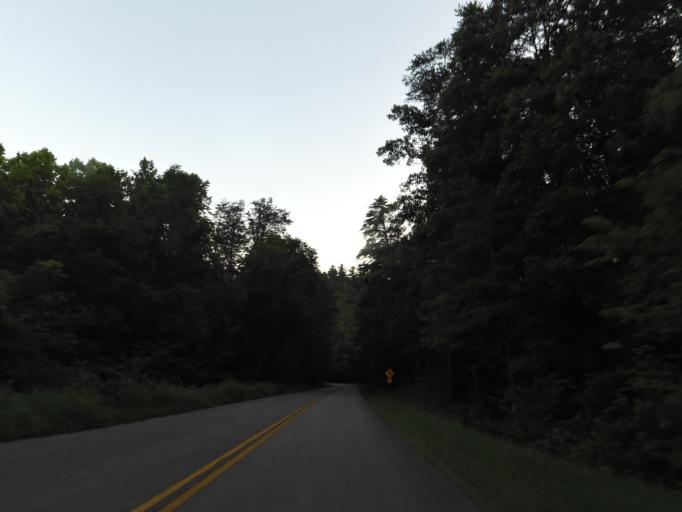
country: US
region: Tennessee
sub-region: Blount County
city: Maryville
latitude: 35.5781
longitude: -84.0025
